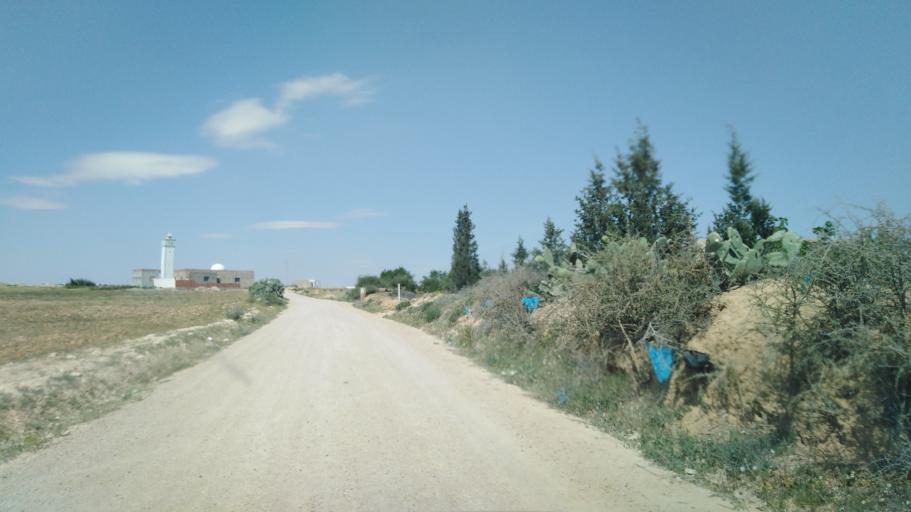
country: TN
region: Safaqis
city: Sfax
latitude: 34.7591
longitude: 10.5279
